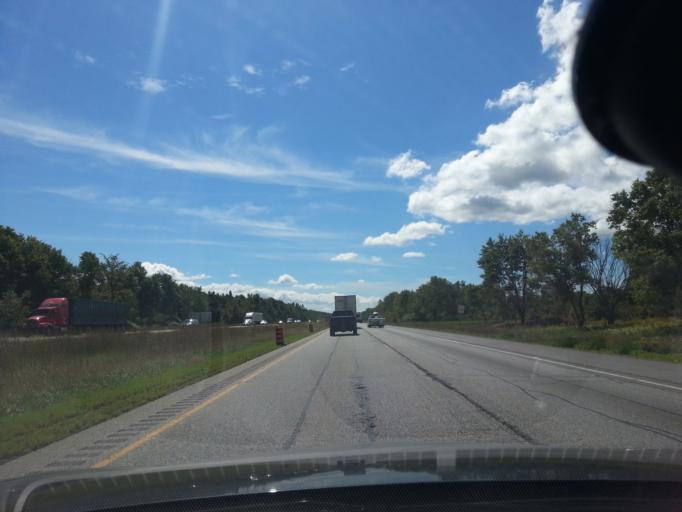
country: US
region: New York
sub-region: Jefferson County
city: Alexandria Bay
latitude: 44.4712
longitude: -75.8722
